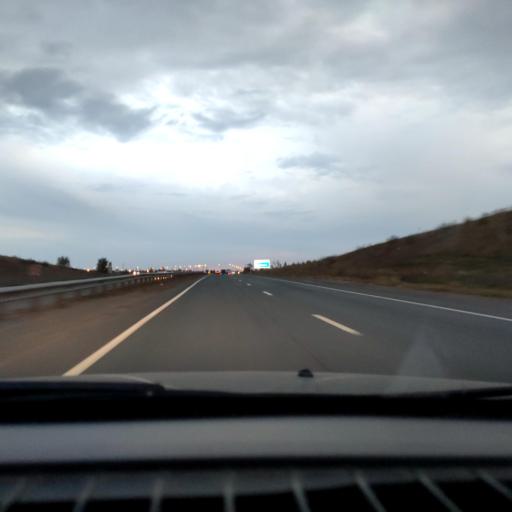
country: RU
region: Samara
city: Zhigulevsk
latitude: 53.5083
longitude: 49.5381
